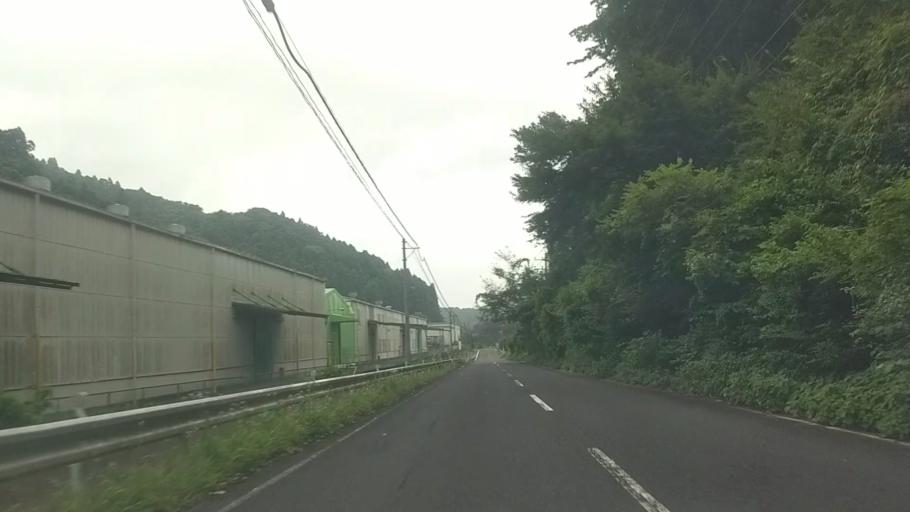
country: JP
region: Chiba
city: Katsuura
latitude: 35.2504
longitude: 140.2438
